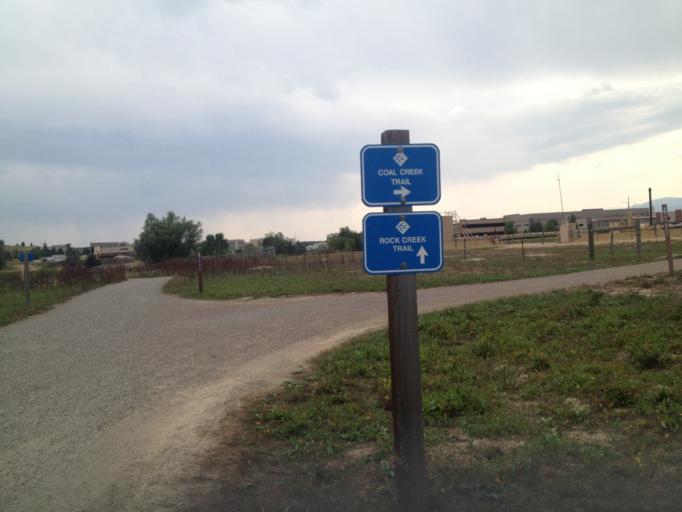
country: US
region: Colorado
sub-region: Boulder County
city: Lafayette
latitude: 39.9838
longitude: -105.0668
